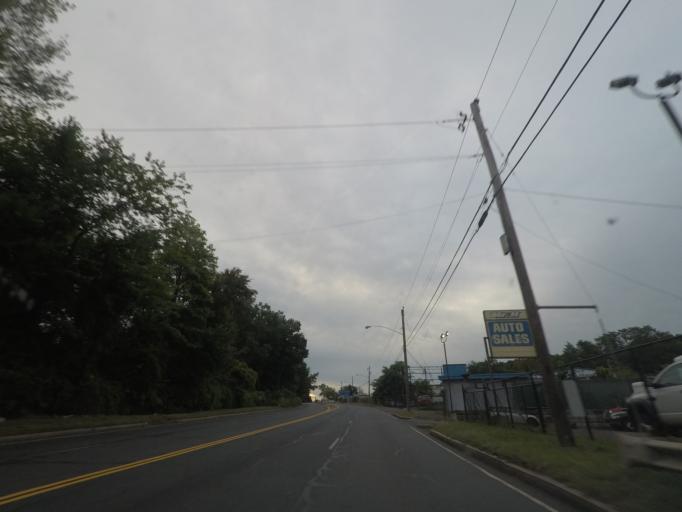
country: US
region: Massachusetts
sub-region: Hampden County
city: Ludlow
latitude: 42.1496
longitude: -72.5231
